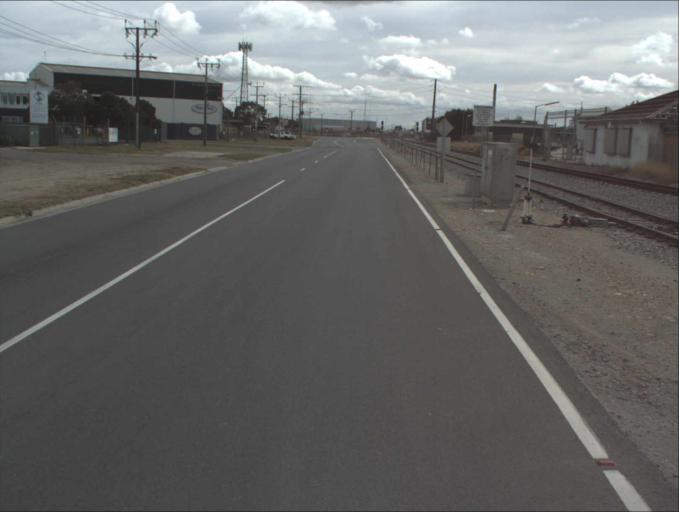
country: AU
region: South Australia
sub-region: Port Adelaide Enfield
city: Birkenhead
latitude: -34.8241
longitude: 138.5053
